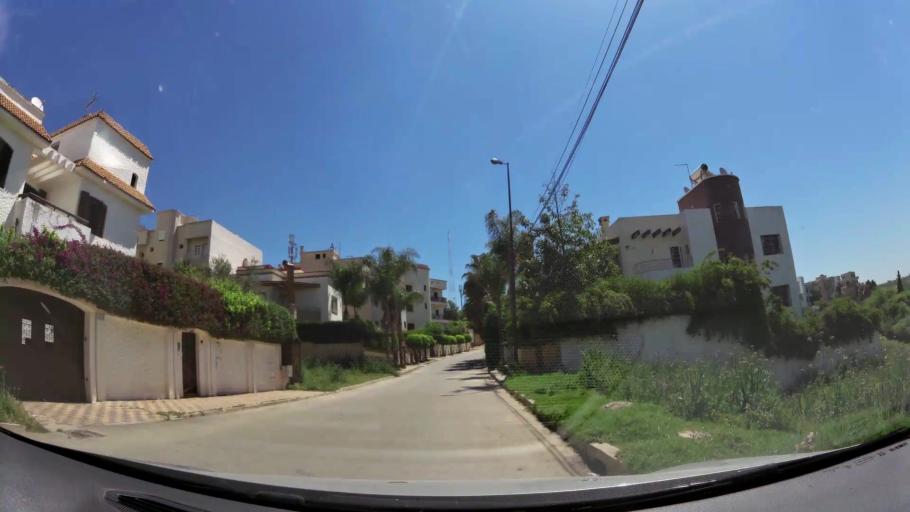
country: MA
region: Meknes-Tafilalet
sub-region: Meknes
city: Meknes
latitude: 33.8870
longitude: -5.5427
